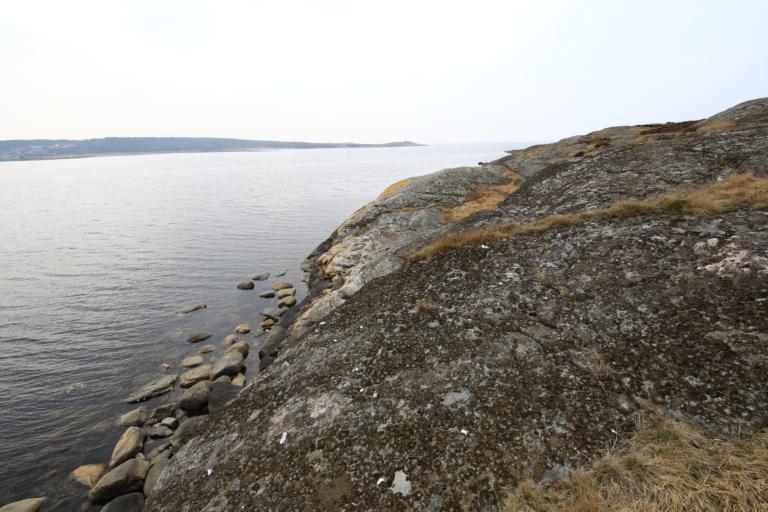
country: SE
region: Halland
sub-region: Kungsbacka Kommun
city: Frillesas
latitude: 57.2475
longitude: 12.1035
